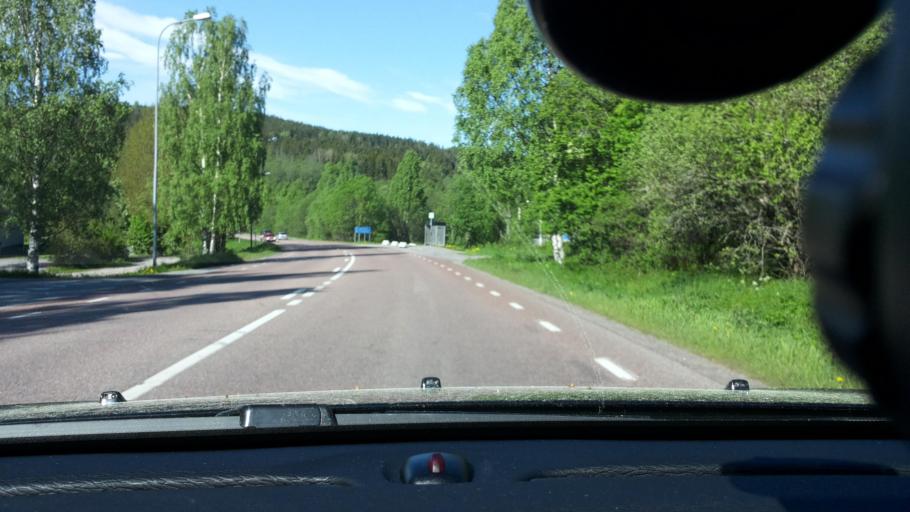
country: SE
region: Vaesternorrland
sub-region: Sundsvalls Kommun
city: Johannedal
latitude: 62.4322
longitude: 17.3860
